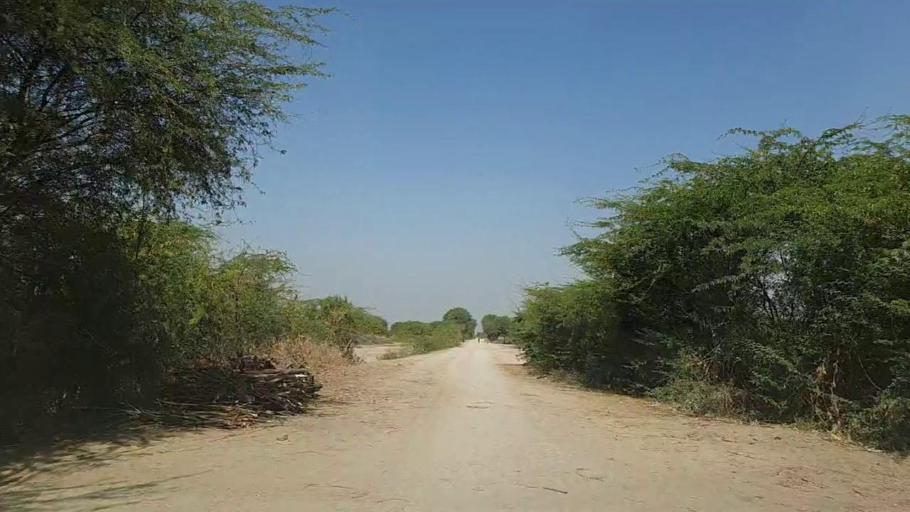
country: PK
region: Sindh
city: Samaro
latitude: 25.1872
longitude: 69.4041
